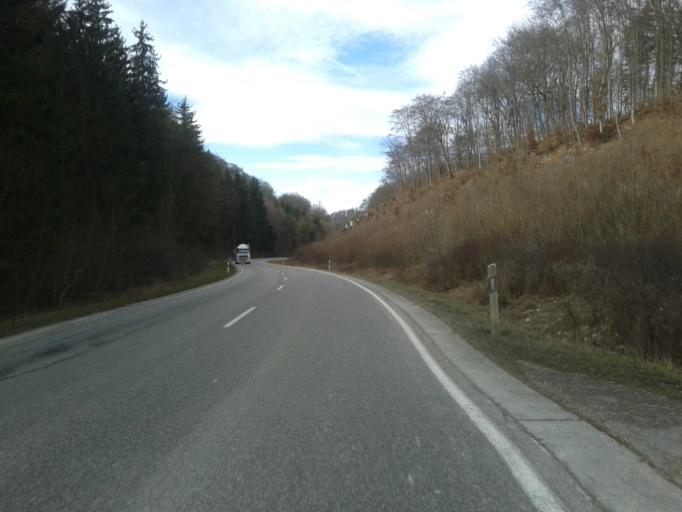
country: DE
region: Baden-Wuerttemberg
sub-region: Tuebingen Region
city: Altheim
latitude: 48.3503
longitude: 9.7768
